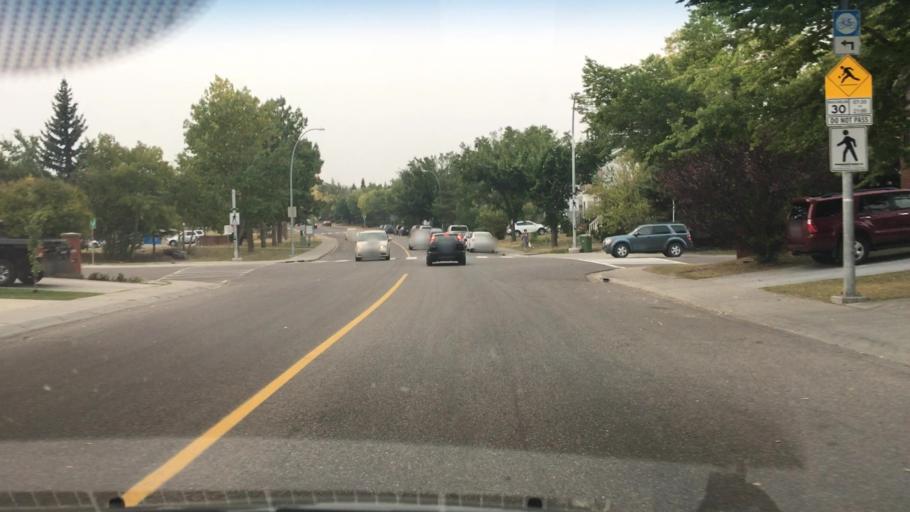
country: CA
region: Alberta
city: Calgary
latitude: 51.1514
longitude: -114.1088
